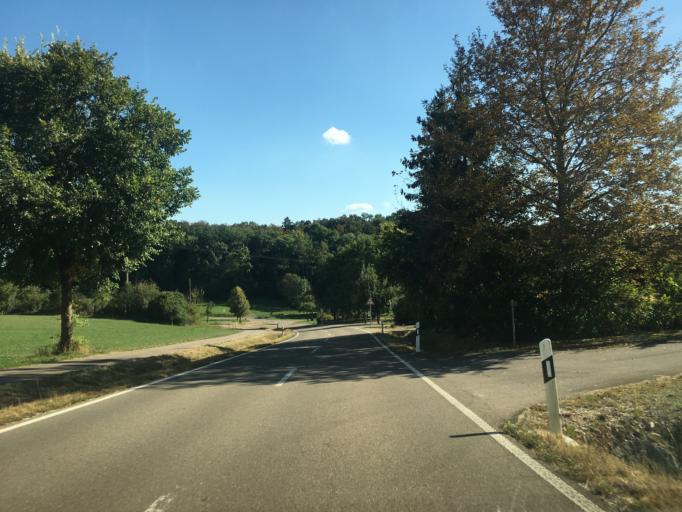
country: DE
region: Baden-Wuerttemberg
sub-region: Tuebingen Region
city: Rechtenstein
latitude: 48.2445
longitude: 9.5484
